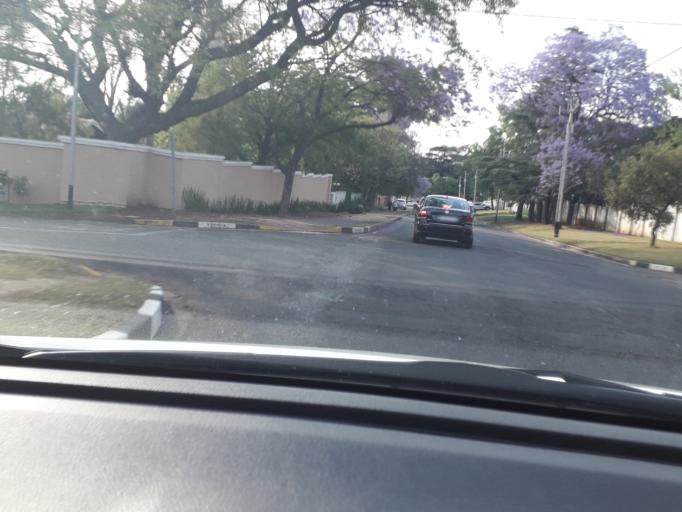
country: ZA
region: Gauteng
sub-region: City of Johannesburg Metropolitan Municipality
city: Johannesburg
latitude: -26.1289
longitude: 27.9918
